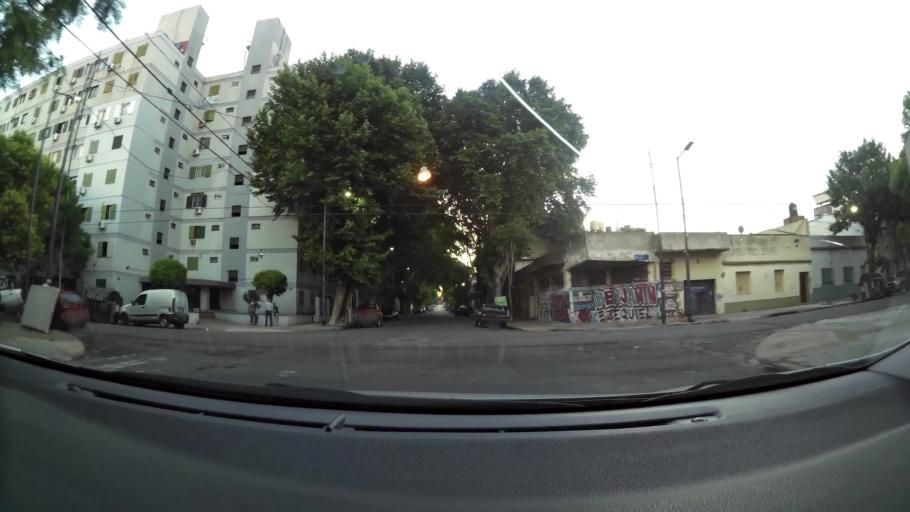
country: AR
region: Buenos Aires F.D.
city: Villa Lugano
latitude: -34.6406
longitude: -58.4386
